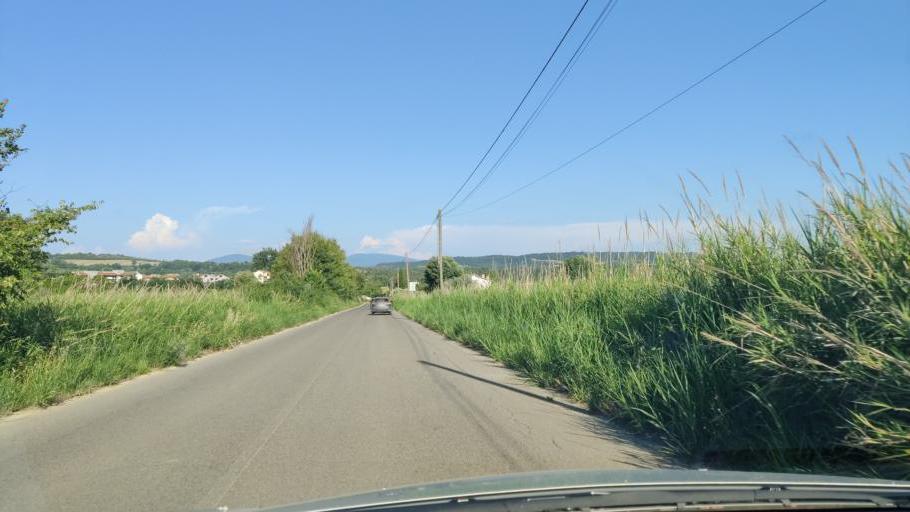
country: IT
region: Latium
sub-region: Provincia di Viterbo
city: Orte
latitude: 42.4694
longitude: 12.3848
